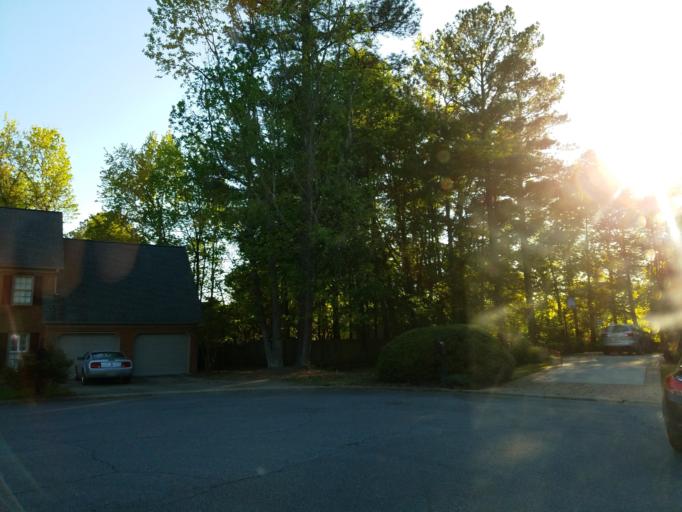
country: US
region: Georgia
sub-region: Cobb County
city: Powder Springs
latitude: 33.9211
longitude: -84.6397
